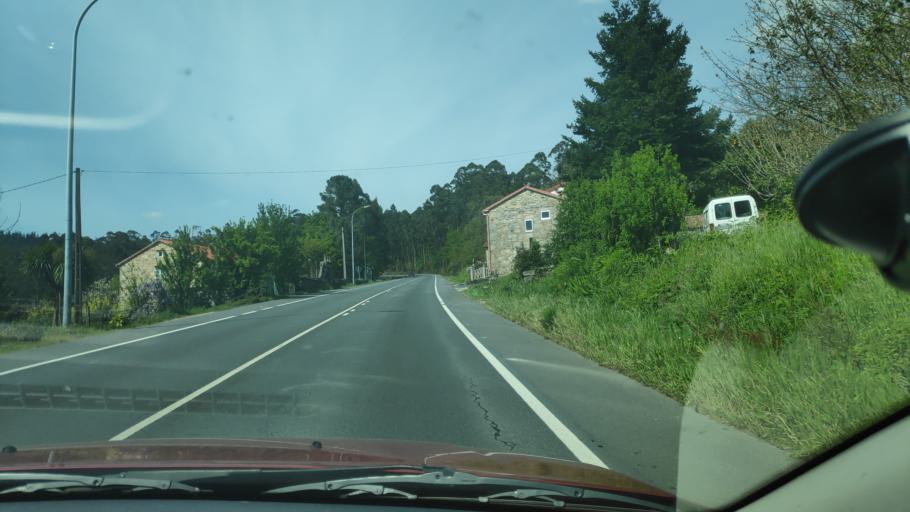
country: ES
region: Galicia
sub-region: Provincia da Coruna
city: Ames
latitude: 42.8719
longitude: -8.6588
